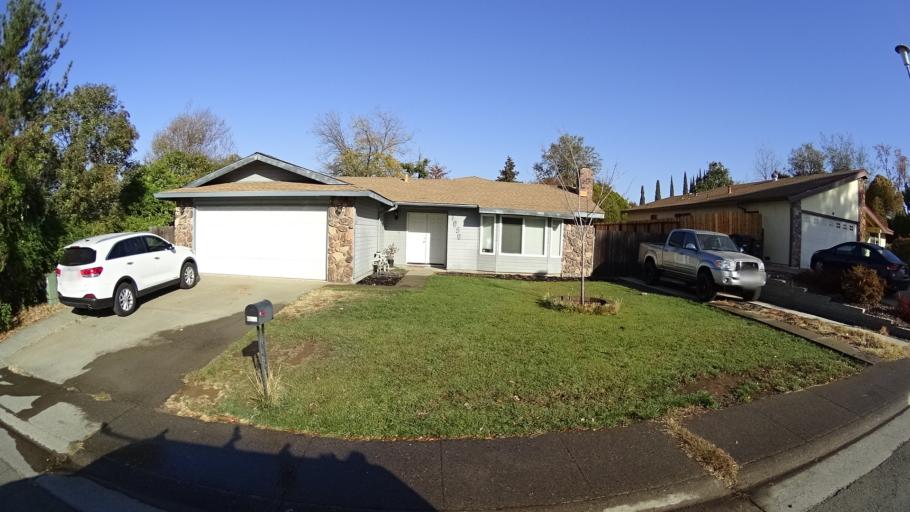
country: US
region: California
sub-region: Sacramento County
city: Citrus Heights
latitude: 38.6943
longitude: -121.2737
